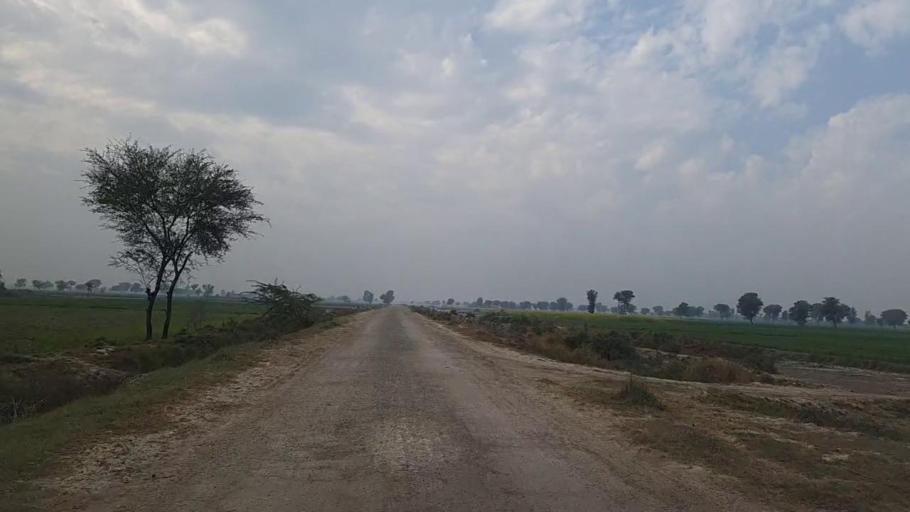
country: PK
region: Sindh
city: Nawabshah
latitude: 26.3652
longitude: 68.4002
